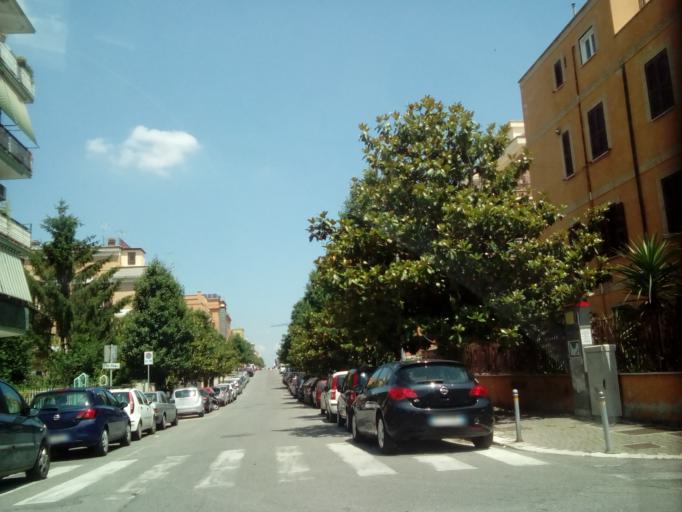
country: IT
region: Latium
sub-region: Citta metropolitana di Roma Capitale
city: Rome
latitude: 41.8780
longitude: 12.5690
